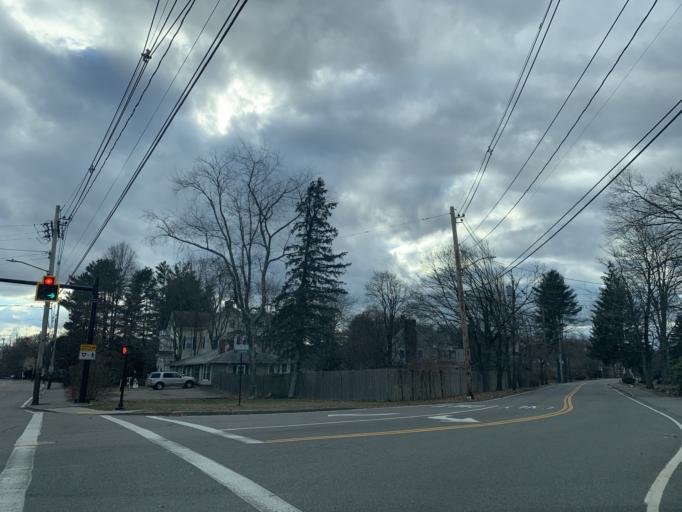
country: US
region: Massachusetts
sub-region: Norfolk County
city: Canton
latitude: 42.1712
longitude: -71.1410
